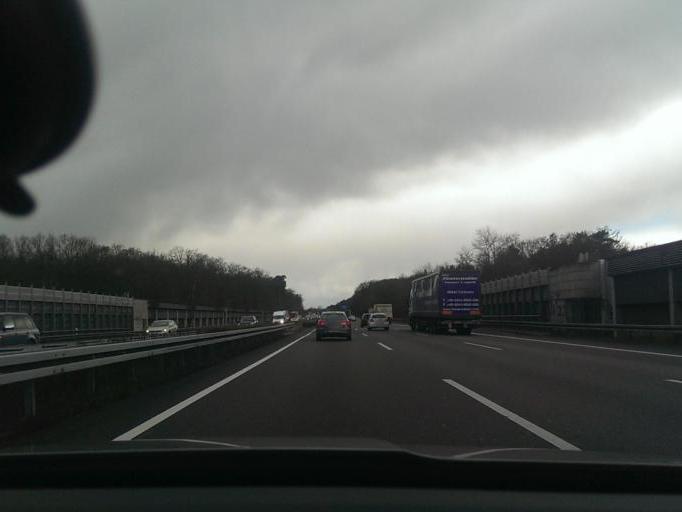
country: DE
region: Lower Saxony
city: Braunschweig
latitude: 52.3119
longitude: 10.5841
